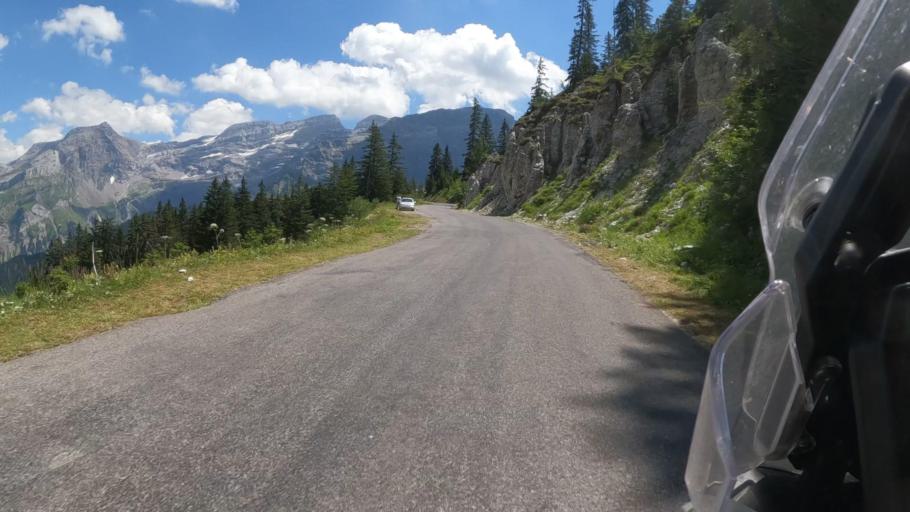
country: CH
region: Vaud
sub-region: Aigle District
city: Villars-sur-Ollon
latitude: 46.3269
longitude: 7.1246
